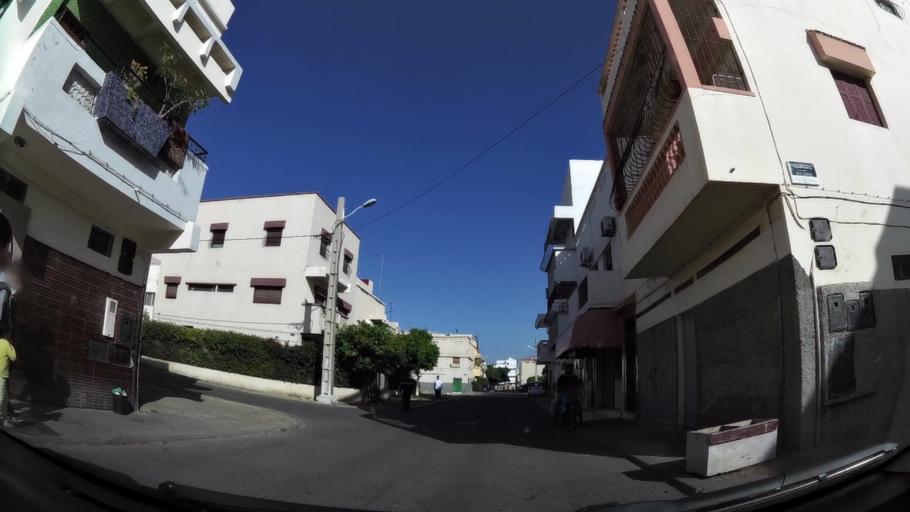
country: MA
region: Souss-Massa-Draa
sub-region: Agadir-Ida-ou-Tnan
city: Agadir
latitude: 30.4327
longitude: -9.5785
